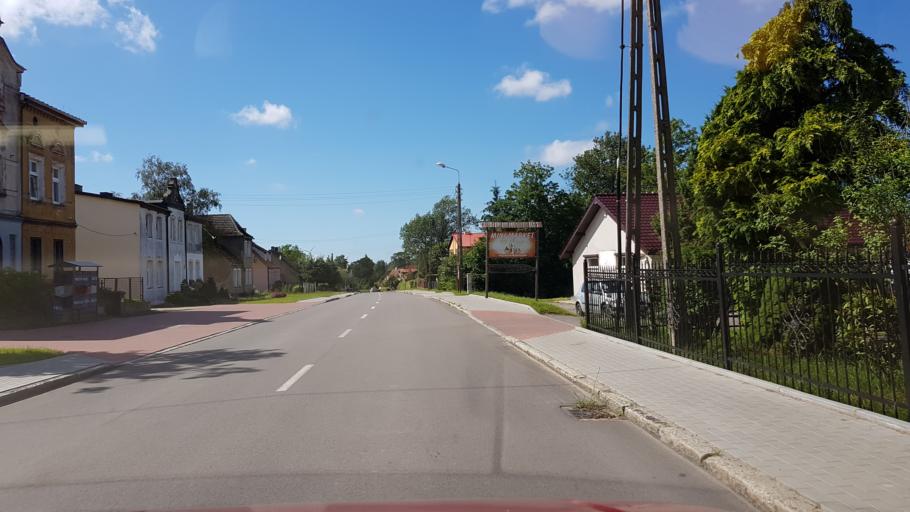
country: PL
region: West Pomeranian Voivodeship
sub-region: Powiat bialogardzki
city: Karlino
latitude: 54.1853
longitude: 15.9209
